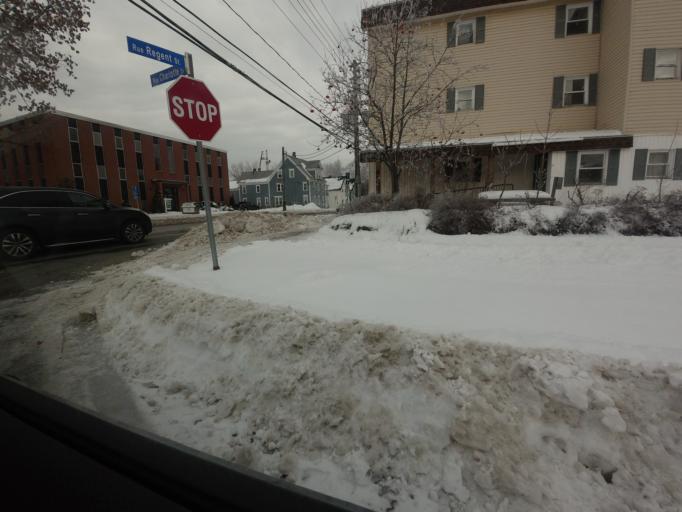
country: CA
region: New Brunswick
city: Fredericton
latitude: 45.9574
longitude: -66.6418
